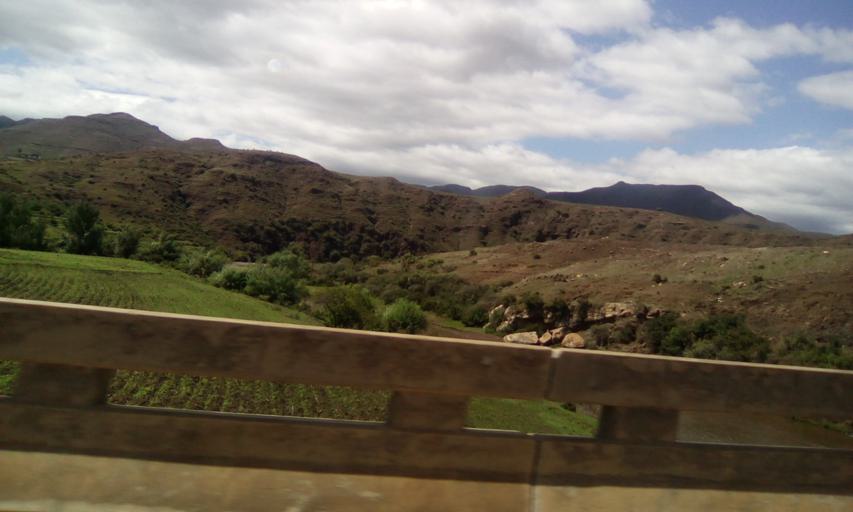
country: LS
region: Maseru
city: Nako
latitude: -29.6633
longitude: 27.8053
